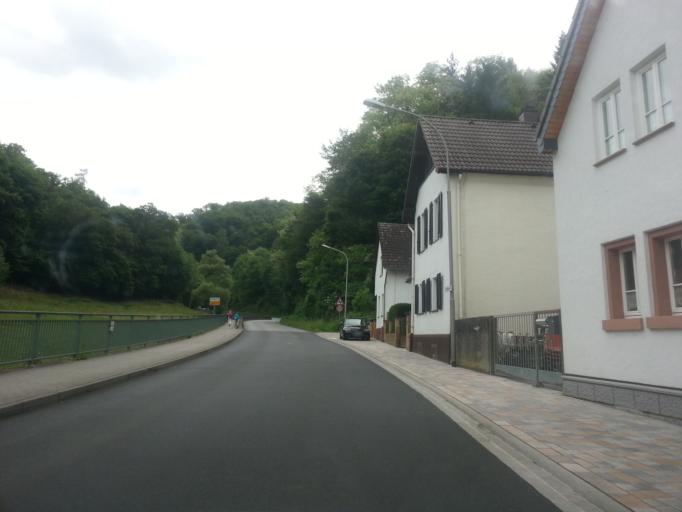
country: DE
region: Hesse
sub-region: Regierungsbezirk Darmstadt
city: Seeheim-Jugenheim
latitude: 49.7509
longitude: 8.6409
